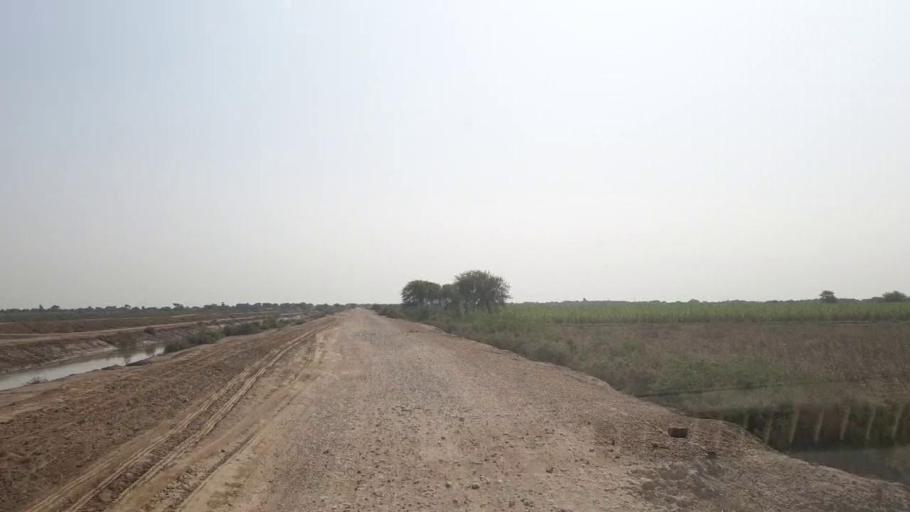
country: PK
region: Sindh
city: Kadhan
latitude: 24.4714
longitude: 68.9038
